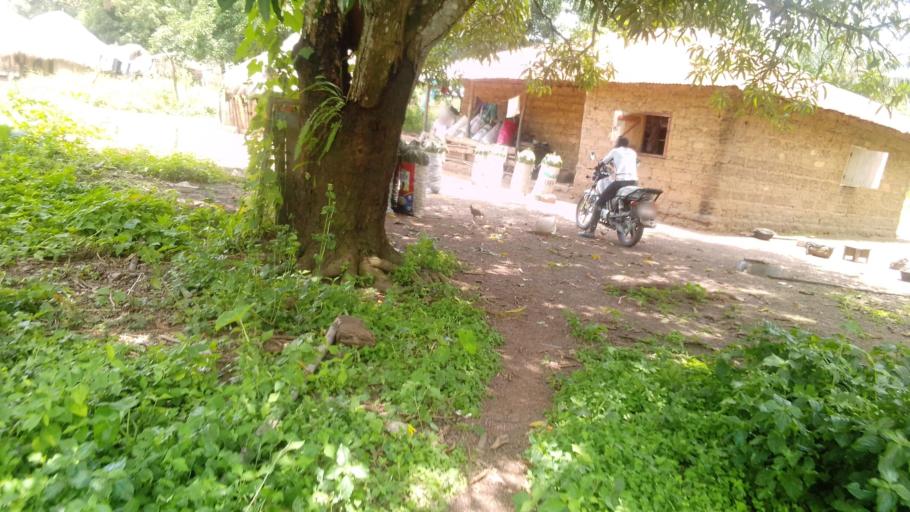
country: SL
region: Northern Province
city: Makeni
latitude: 9.0521
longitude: -12.1864
